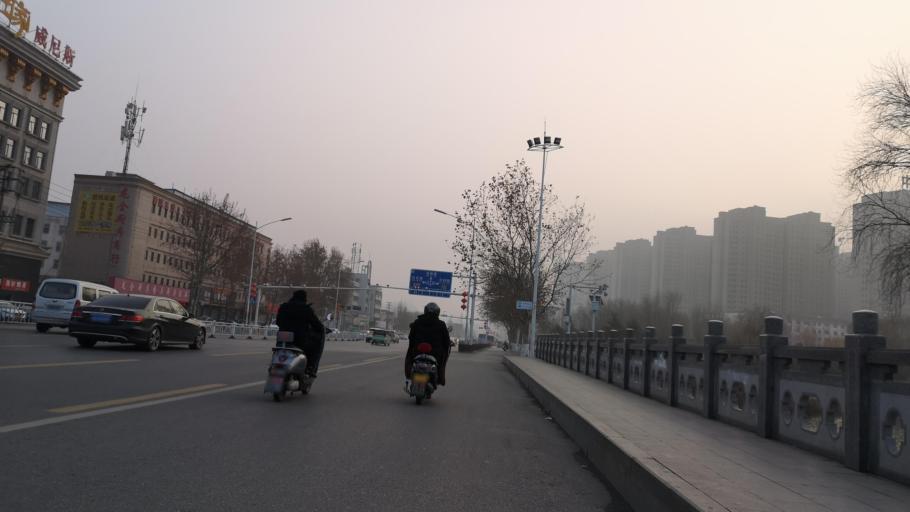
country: CN
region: Henan Sheng
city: Puyang
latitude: 35.7506
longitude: 115.0299
